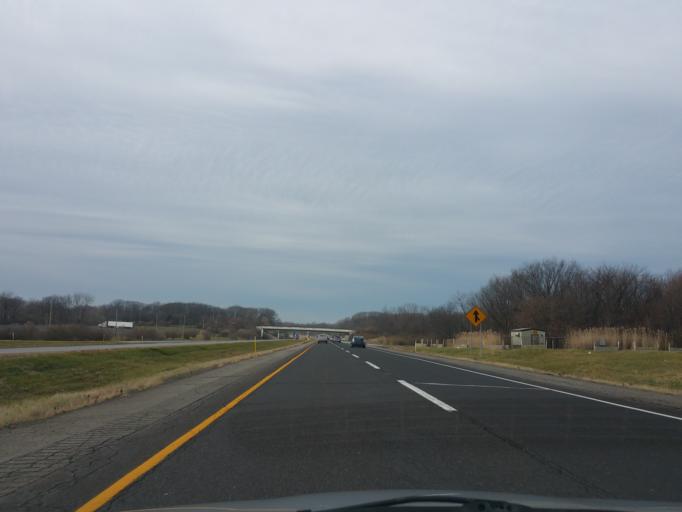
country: US
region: Indiana
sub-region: LaPorte County
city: Westville
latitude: 41.5865
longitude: -86.9254
